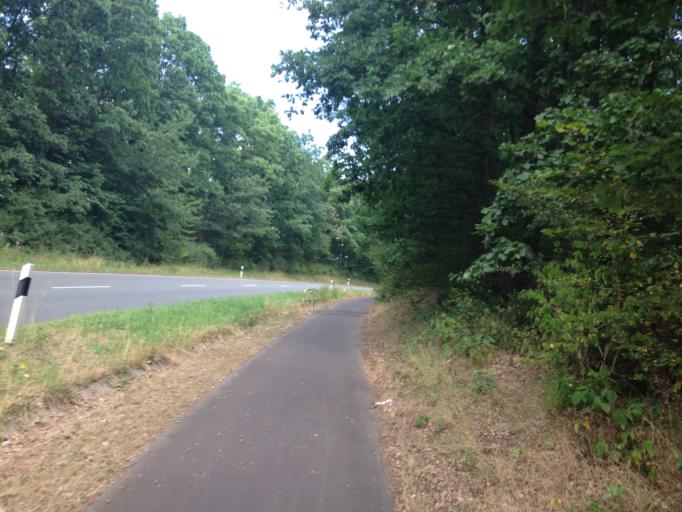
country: DE
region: Hesse
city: Allendorf an der Lahn
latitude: 50.5500
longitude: 8.6348
